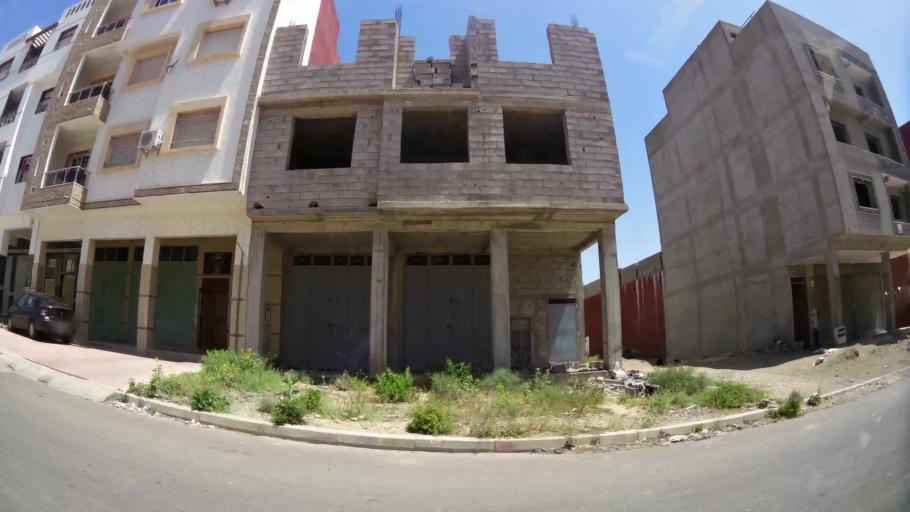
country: MA
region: Oued ed Dahab-Lagouira
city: Dakhla
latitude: 30.4380
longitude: -9.5553
